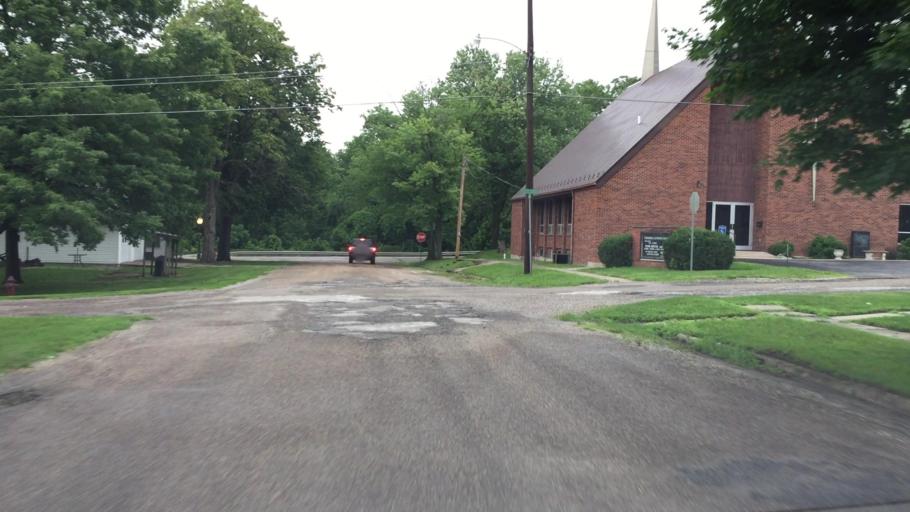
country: US
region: Illinois
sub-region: Hancock County
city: Warsaw
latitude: 40.3576
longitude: -91.4324
